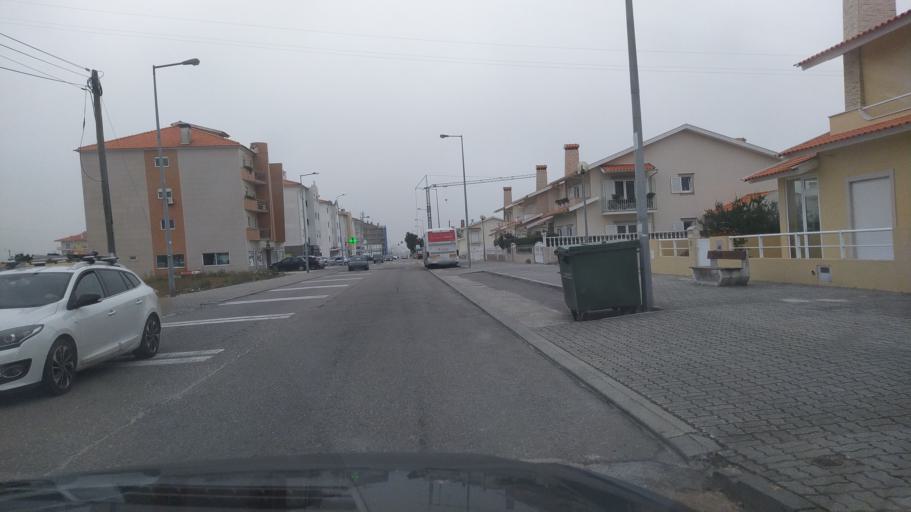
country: PT
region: Aveiro
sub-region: Ilhavo
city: Gafanha da Encarnacao
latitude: 40.5586
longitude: -8.7497
